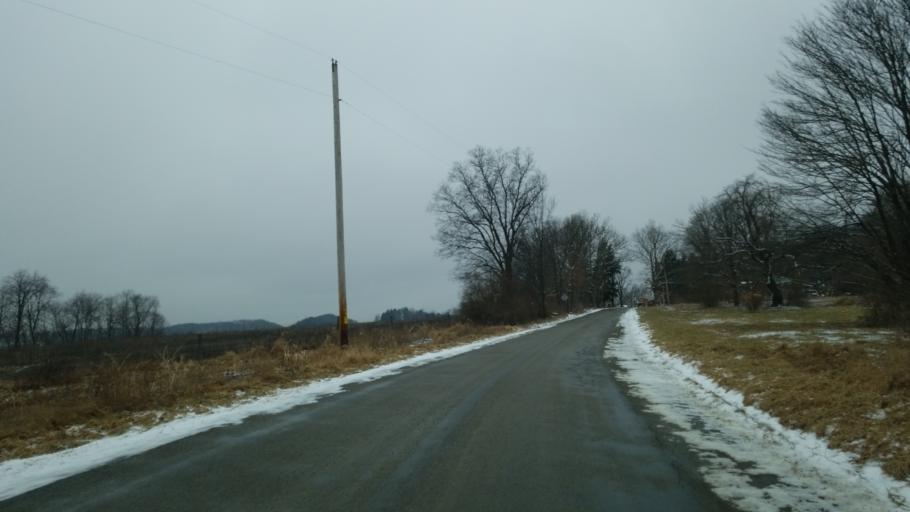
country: US
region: Pennsylvania
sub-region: Jefferson County
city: Sykesville
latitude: 41.0810
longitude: -78.8089
